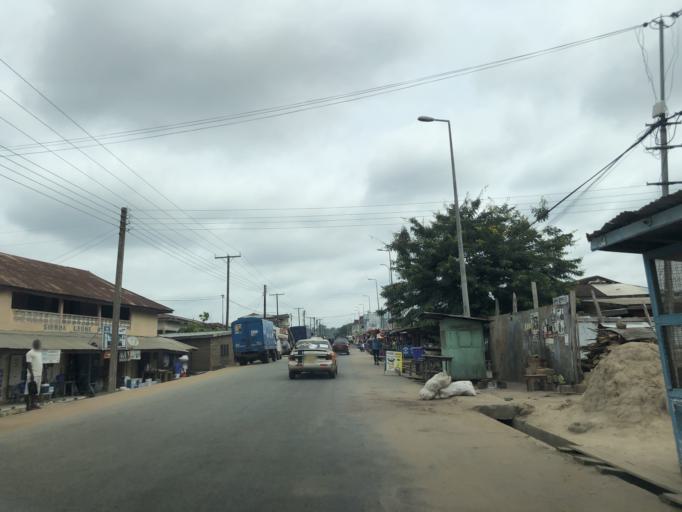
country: GH
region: Eastern
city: Koforidua
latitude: 6.1140
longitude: -0.2705
